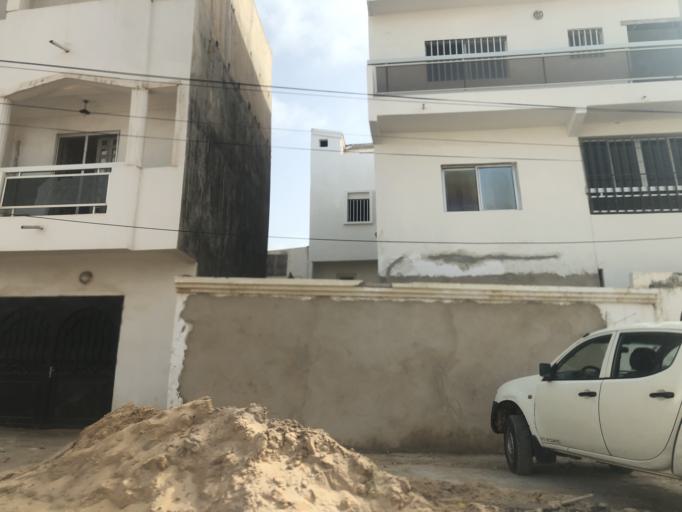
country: SN
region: Dakar
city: Mermoz Boabab
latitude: 14.7332
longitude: -17.4971
